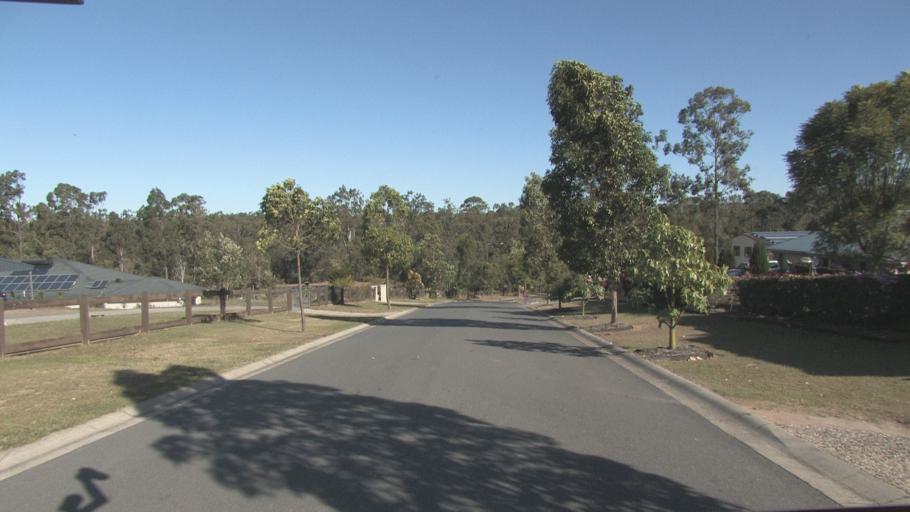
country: AU
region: Queensland
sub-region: Ipswich
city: Springfield Lakes
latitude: -27.7235
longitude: 152.9246
